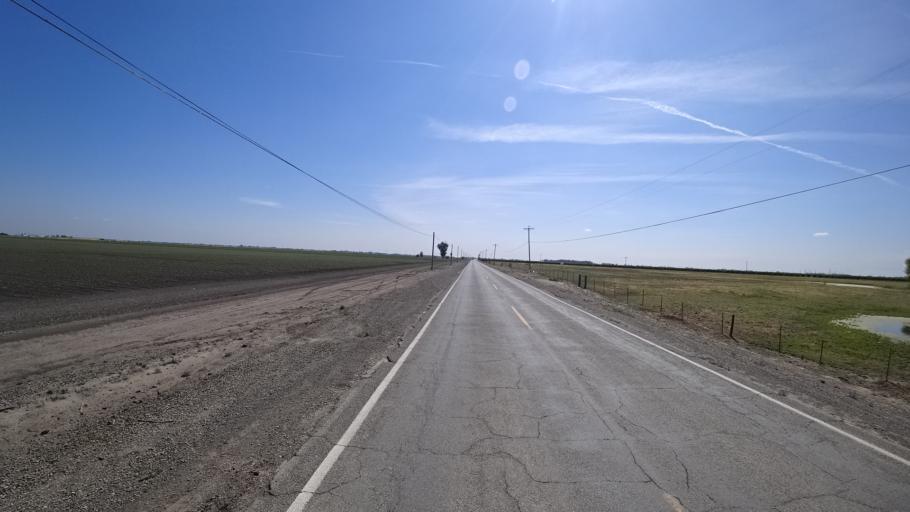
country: US
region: California
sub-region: Kings County
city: Lemoore Station
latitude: 36.2554
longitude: -119.8489
